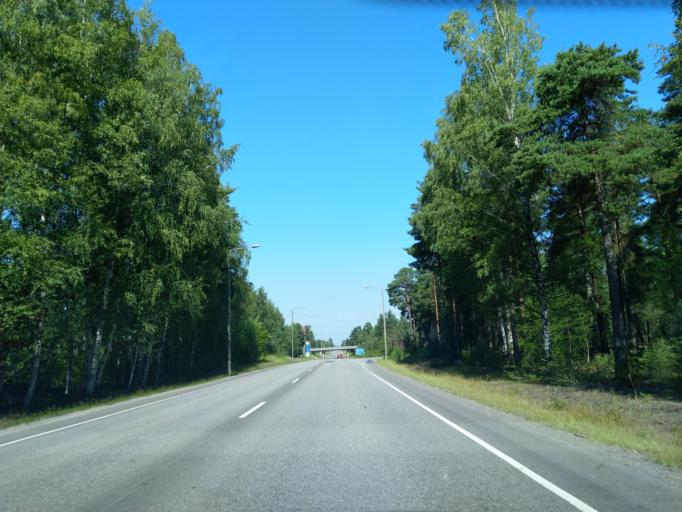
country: FI
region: Satakunta
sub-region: Pori
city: Harjavalta
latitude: 61.3040
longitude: 22.1349
